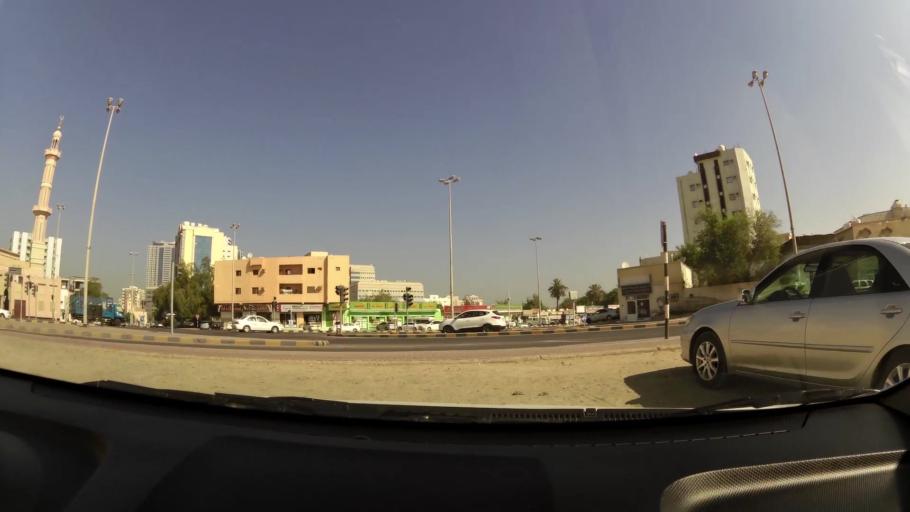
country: AE
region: Ajman
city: Ajman
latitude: 25.4147
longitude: 55.4472
